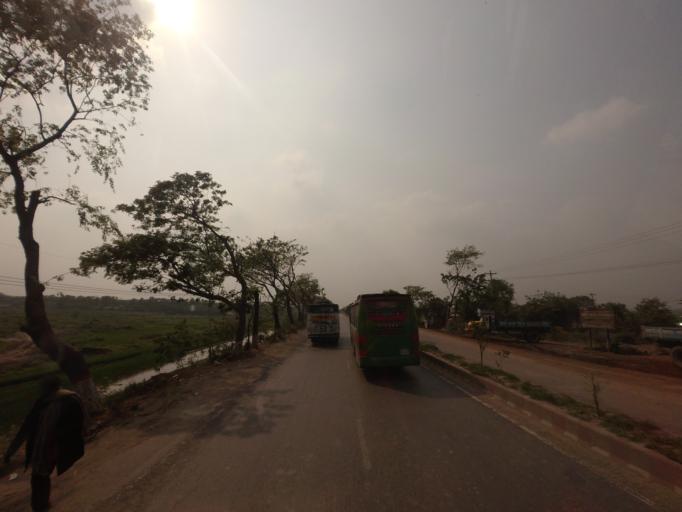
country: BD
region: Dhaka
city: Azimpur
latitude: 23.7907
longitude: 90.3098
